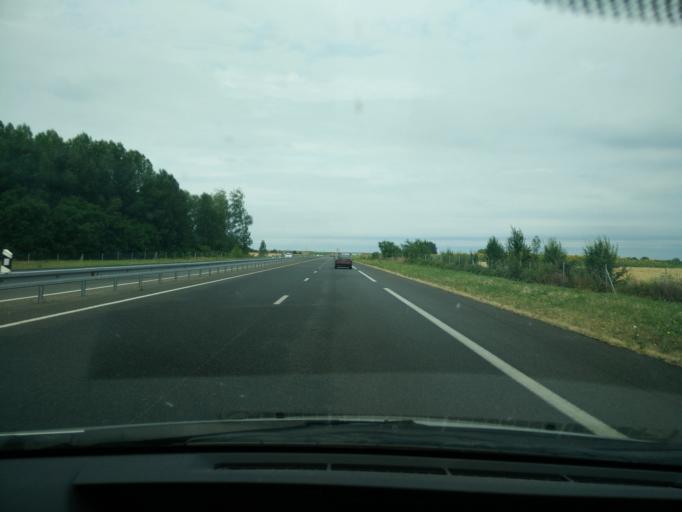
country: FR
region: Pays de la Loire
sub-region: Departement de Maine-et-Loire
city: Saint-Jean
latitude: 47.2861
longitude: -0.3607
